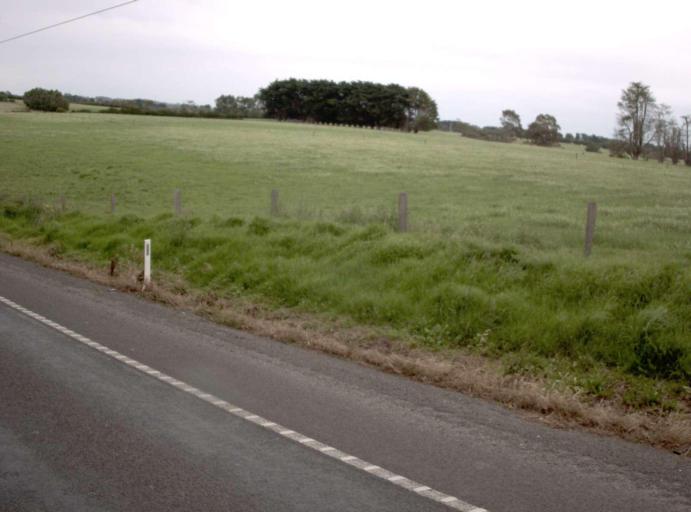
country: AU
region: Victoria
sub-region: Baw Baw
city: Warragul
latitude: -38.5078
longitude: 145.9519
